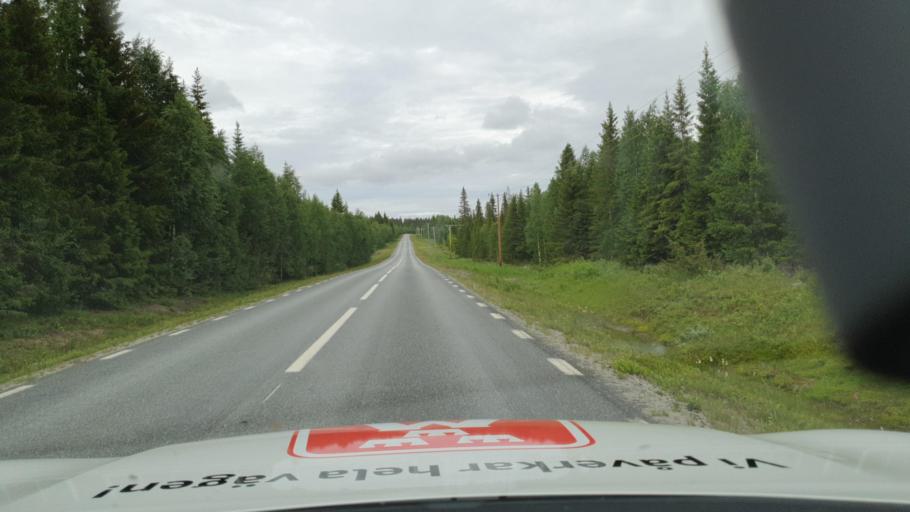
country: SE
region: Vaesterbotten
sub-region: Lycksele Kommun
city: Soderfors
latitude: 64.3752
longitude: 17.9761
